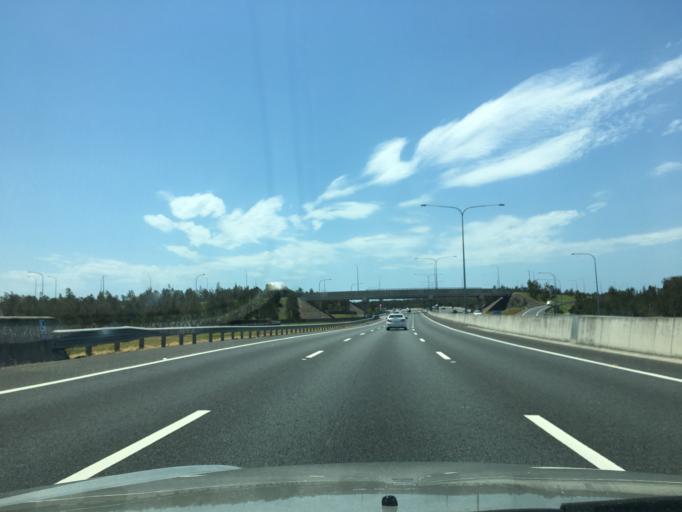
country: AU
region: Queensland
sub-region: Brisbane
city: Ascot
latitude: -27.4080
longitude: 153.0890
